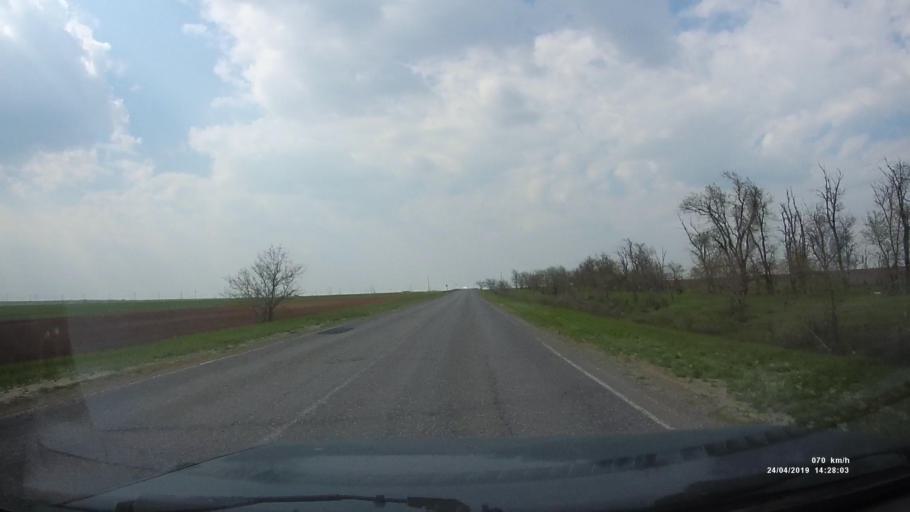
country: RU
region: Kalmykiya
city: Arshan'
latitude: 46.3359
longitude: 44.0339
